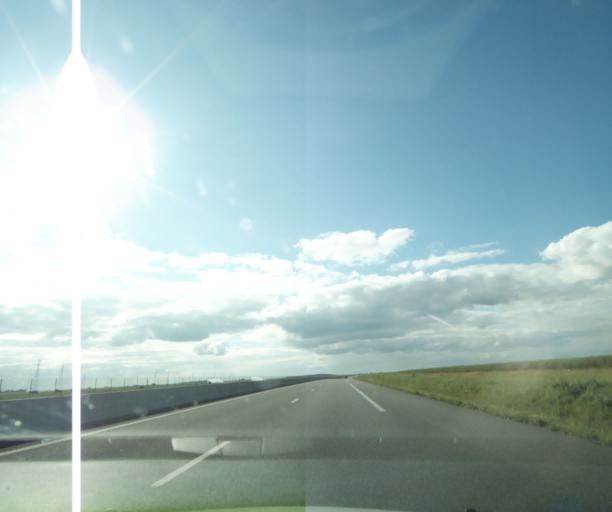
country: FR
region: Centre
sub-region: Departement d'Eure-et-Loir
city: Sours
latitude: 48.3598
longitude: 1.6060
